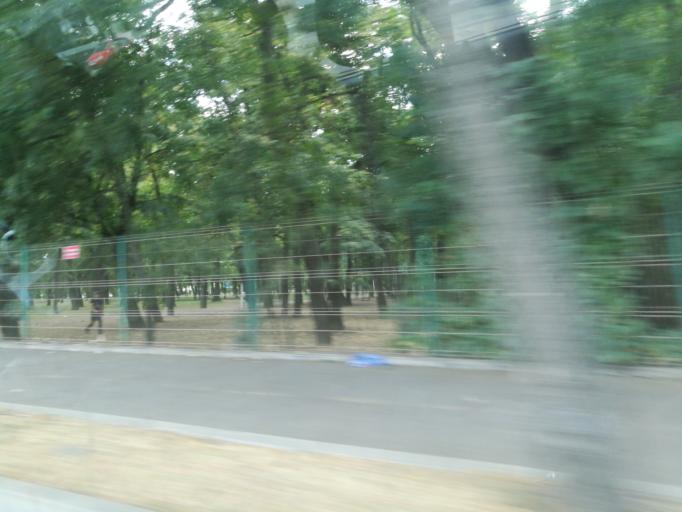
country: RO
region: Ilfov
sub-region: Comuna Chiajna
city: Rosu
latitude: 44.4906
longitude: 26.0347
